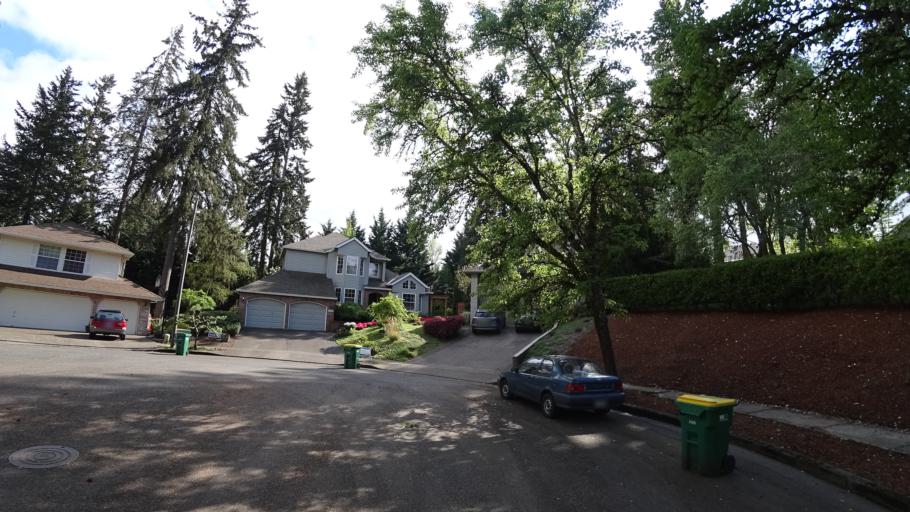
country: US
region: Oregon
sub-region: Washington County
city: Beaverton
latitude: 45.4457
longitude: -122.8315
